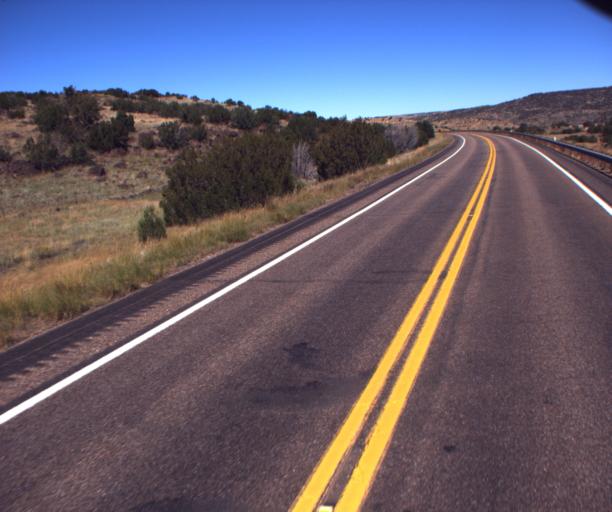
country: US
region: Arizona
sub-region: Apache County
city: Saint Johns
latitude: 34.3487
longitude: -109.3789
